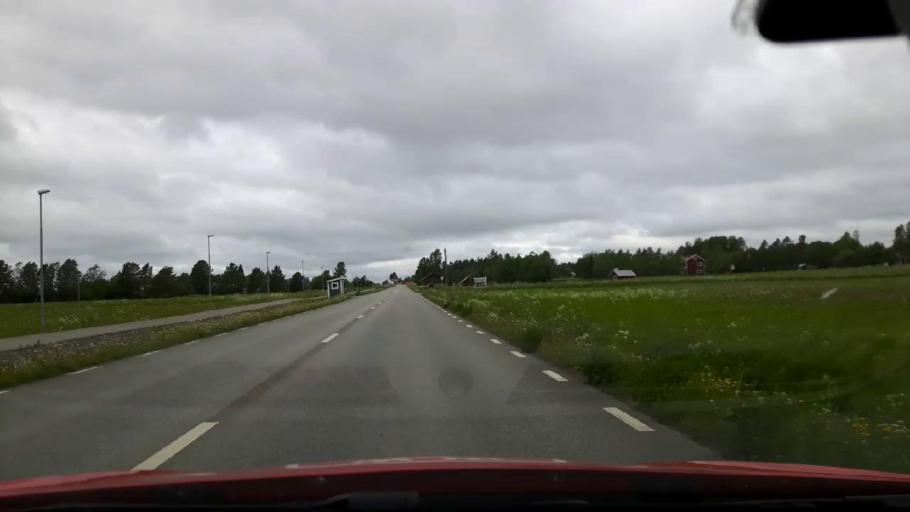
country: SE
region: Jaemtland
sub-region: OEstersunds Kommun
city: Ostersund
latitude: 63.2260
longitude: 14.5945
